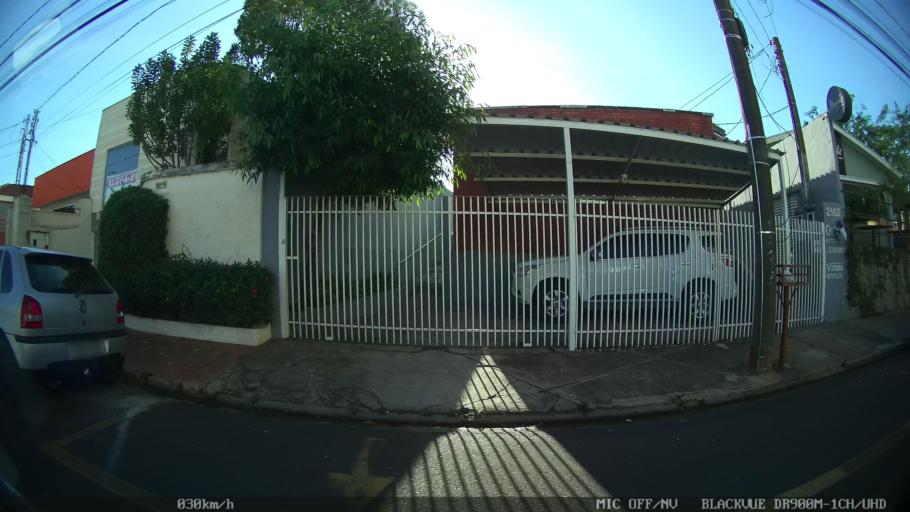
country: BR
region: Sao Paulo
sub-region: Sao Jose Do Rio Preto
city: Sao Jose do Rio Preto
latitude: -20.8151
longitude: -49.3943
